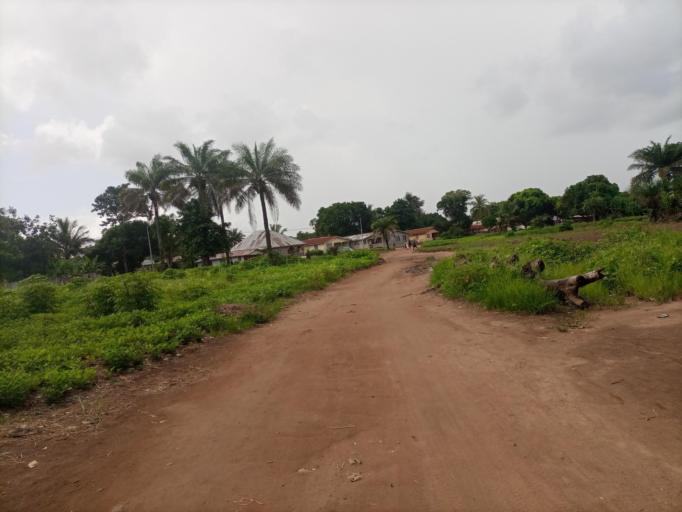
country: SL
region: Northern Province
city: Tintafor
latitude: 8.6298
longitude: -13.2134
